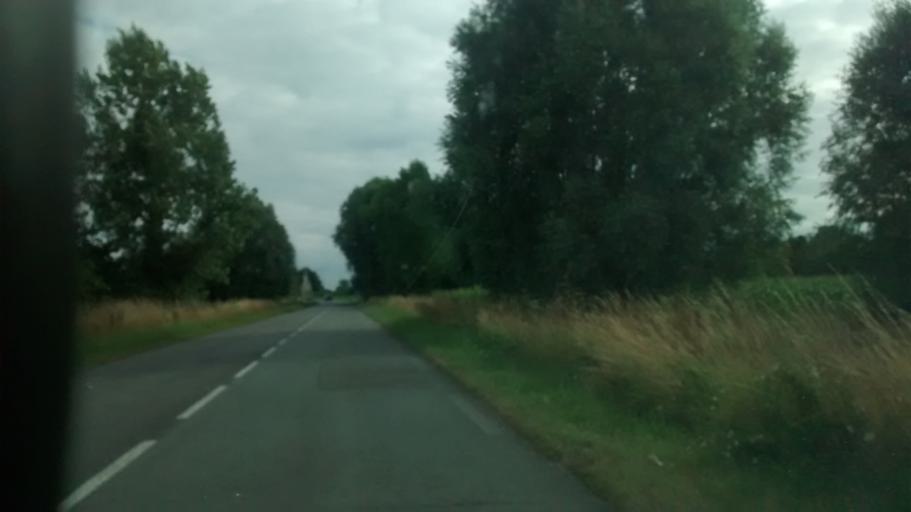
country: FR
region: Brittany
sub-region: Departement d'Ille-et-Vilaine
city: Le Vivier-sur-Mer
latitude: 48.5910
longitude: -1.7762
